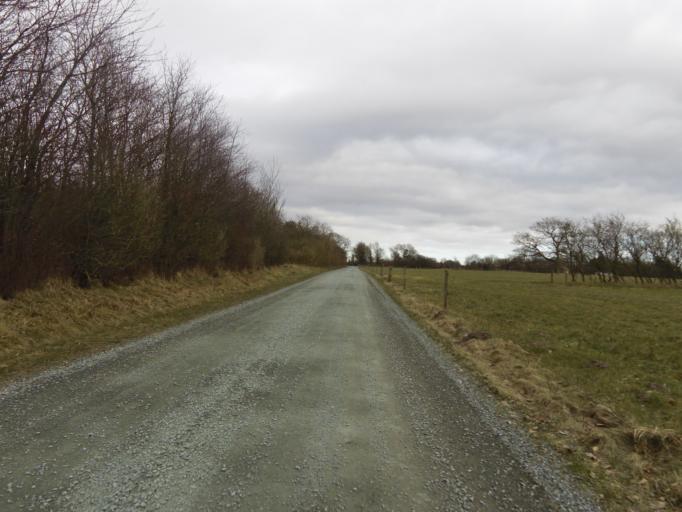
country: DK
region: South Denmark
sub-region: Tonder Kommune
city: Toftlund
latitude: 55.2120
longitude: 9.1699
